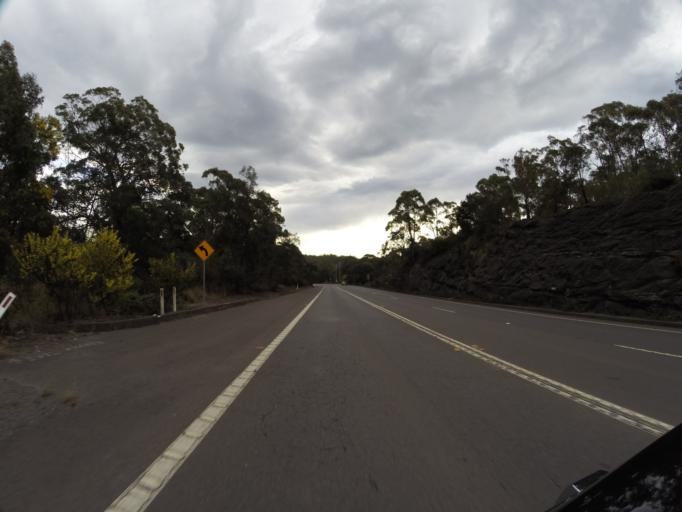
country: AU
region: New South Wales
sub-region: Wollondilly
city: Douglas Park
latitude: -34.2134
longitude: 150.7994
